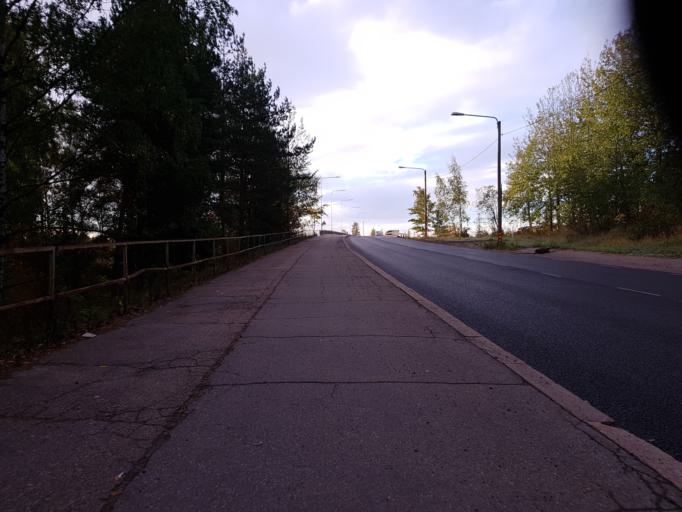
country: FI
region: Uusimaa
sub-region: Helsinki
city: Helsinki
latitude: 60.2190
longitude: 24.9338
